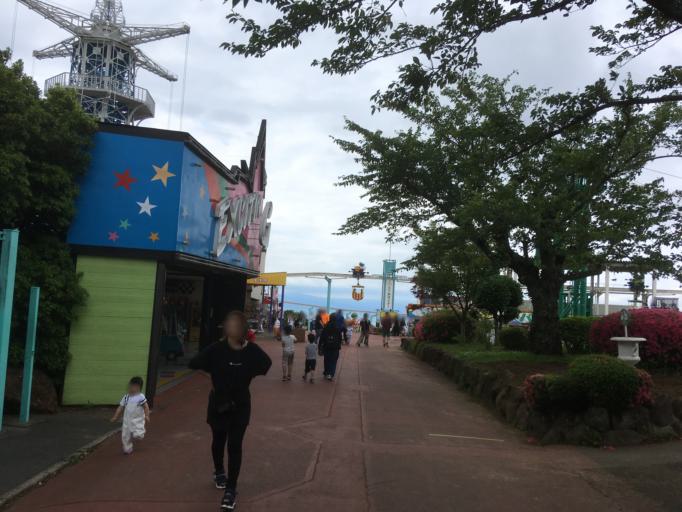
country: JP
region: Nara
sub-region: Ikoma-shi
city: Ikoma
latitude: 34.6784
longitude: 135.6789
